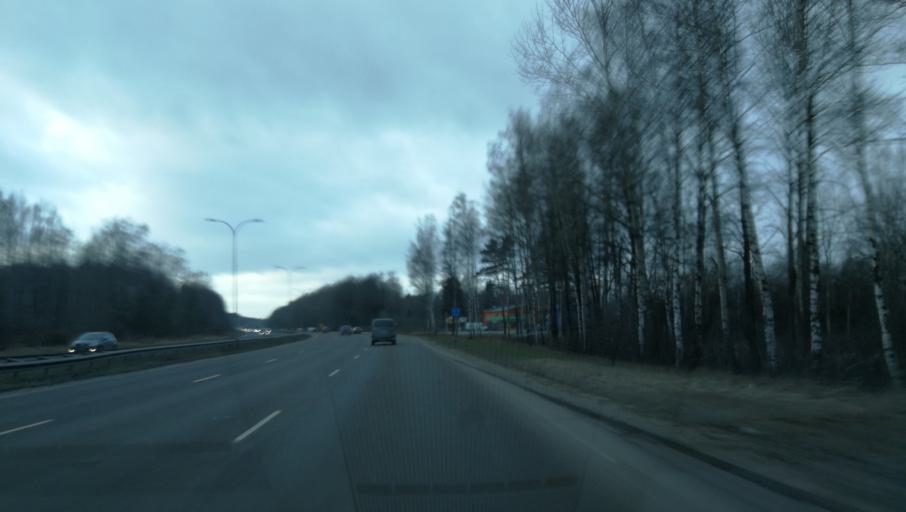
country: LV
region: Babite
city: Pinki
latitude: 56.9503
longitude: 23.9812
